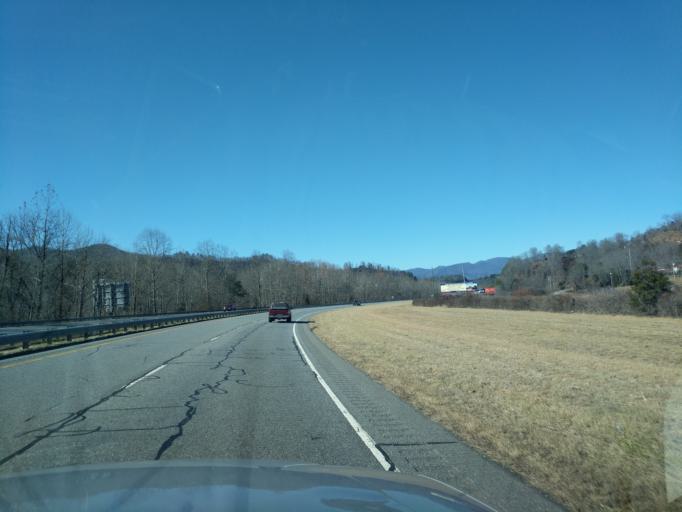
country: US
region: North Carolina
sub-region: Swain County
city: Cherokee
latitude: 35.4223
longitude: -83.3440
